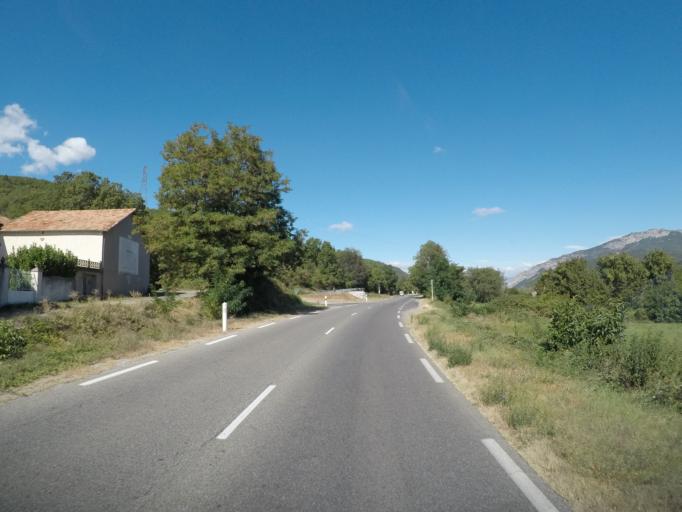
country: FR
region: Provence-Alpes-Cote d'Azur
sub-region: Departement des Alpes-de-Haute-Provence
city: Peipin
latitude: 44.1484
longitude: 5.9595
